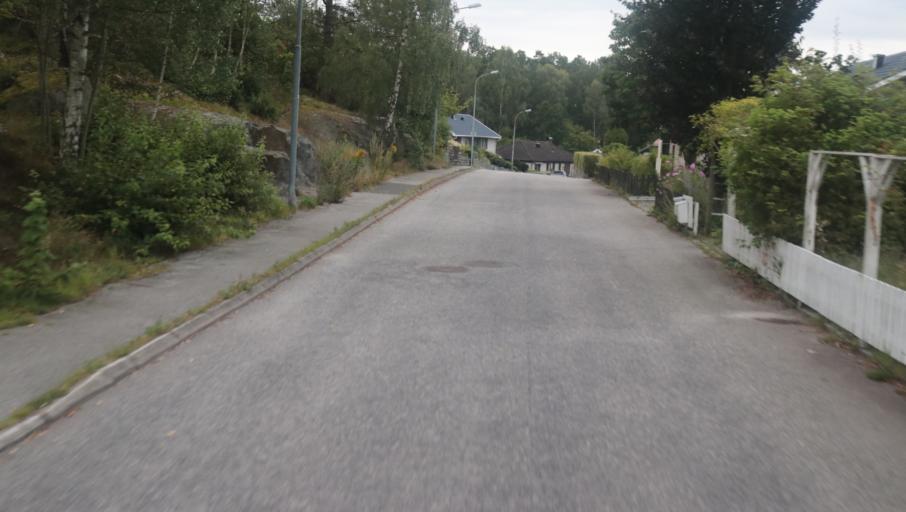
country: SE
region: Blekinge
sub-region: Karlshamns Kommun
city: Karlshamn
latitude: 56.1714
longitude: 14.8860
